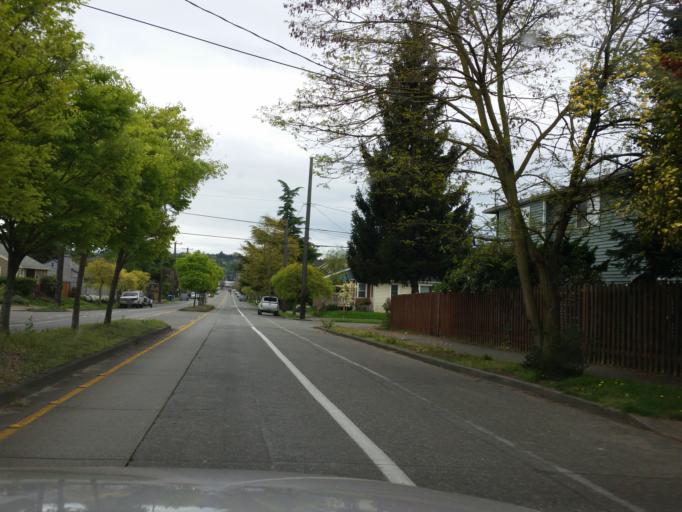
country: US
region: Washington
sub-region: King County
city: Seattle
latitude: 47.6670
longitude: -122.3663
